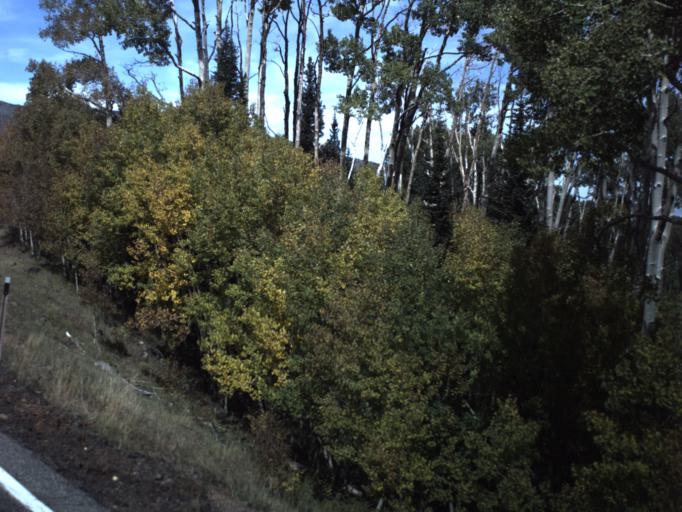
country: US
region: Utah
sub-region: Wayne County
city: Loa
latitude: 38.0709
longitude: -111.3369
